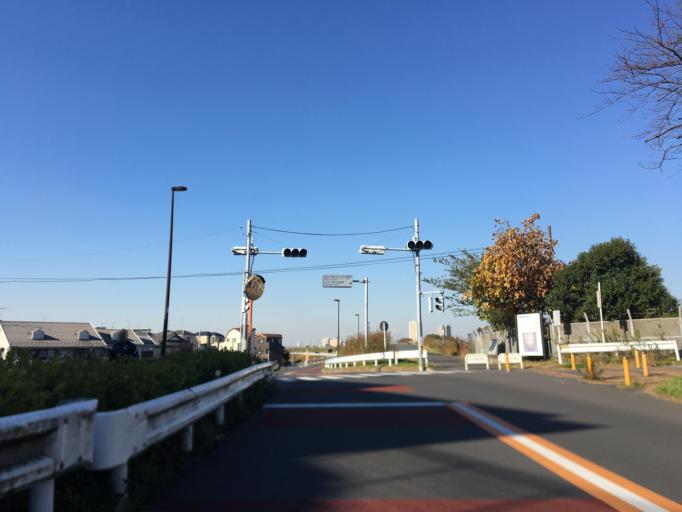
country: JP
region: Tokyo
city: Urayasu
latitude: 35.7017
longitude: 139.9166
